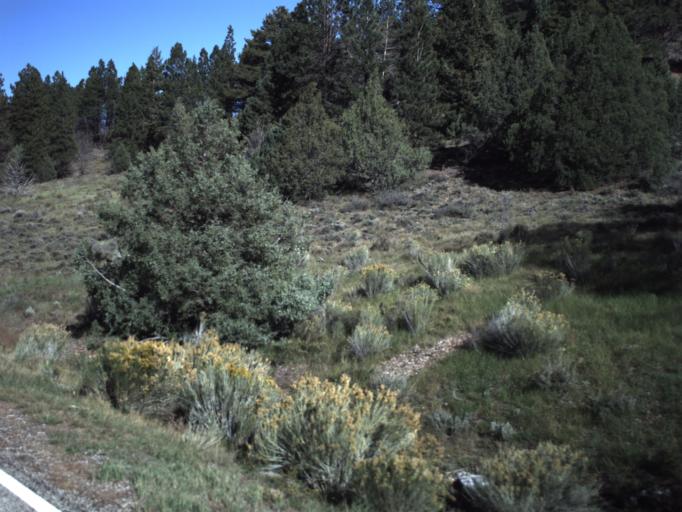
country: US
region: Utah
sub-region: Garfield County
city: Panguitch
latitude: 37.7446
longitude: -112.5881
